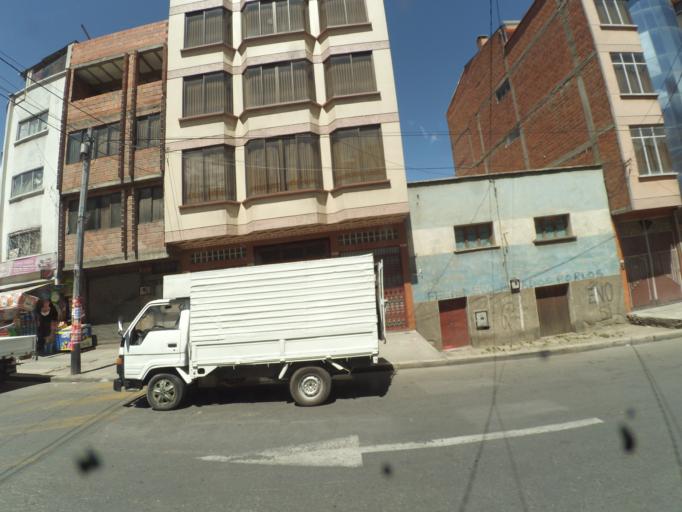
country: BO
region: La Paz
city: La Paz
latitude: -16.4896
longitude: -68.1675
